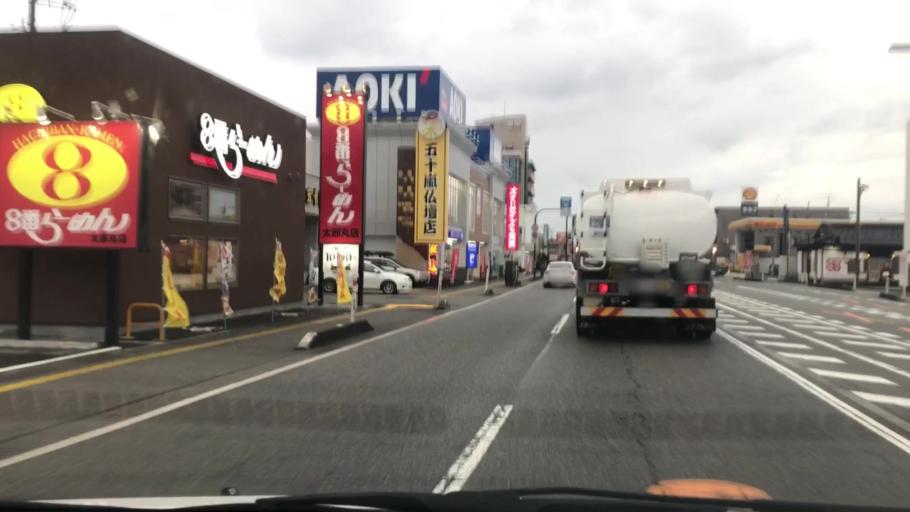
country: JP
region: Toyama
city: Toyama-shi
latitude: 36.6753
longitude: 137.2107
